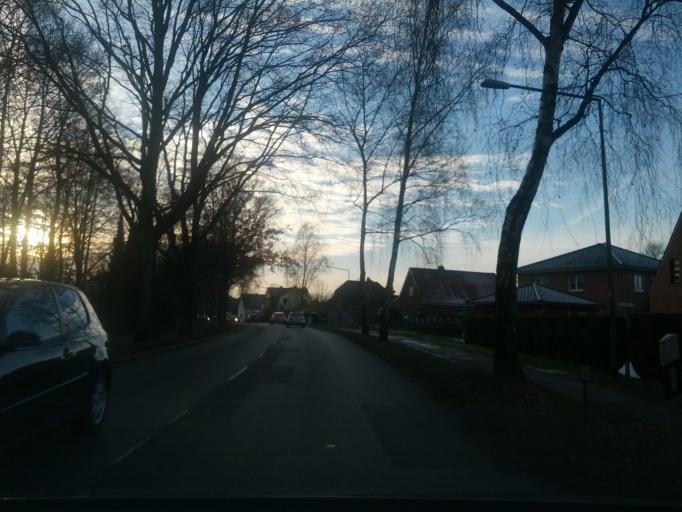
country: DE
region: Lower Saxony
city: Buxtehude
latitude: 53.4633
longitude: 9.6652
